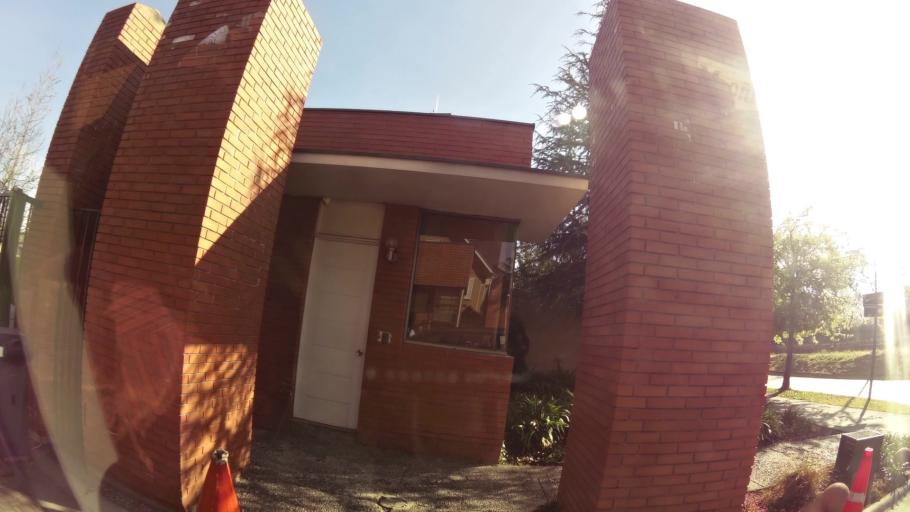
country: CL
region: Santiago Metropolitan
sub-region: Provincia de Santiago
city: Villa Presidente Frei, Nunoa, Santiago, Chile
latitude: -33.4895
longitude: -70.5500
